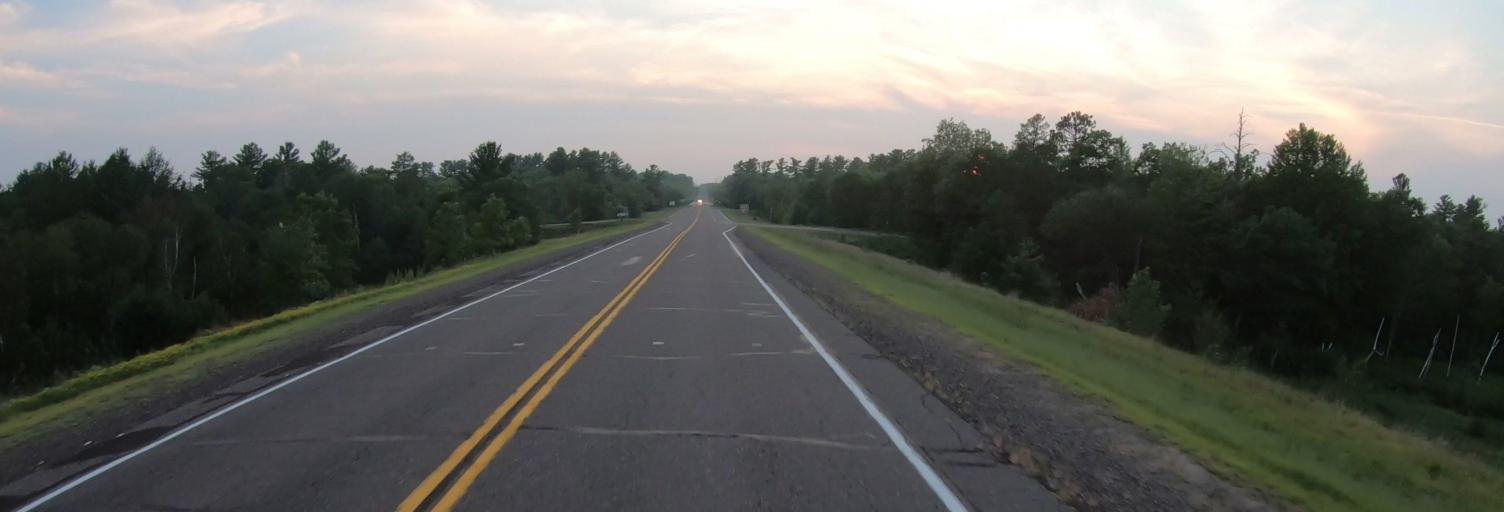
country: US
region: Wisconsin
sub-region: Burnett County
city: Grantsburg
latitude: 45.7732
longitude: -92.7740
